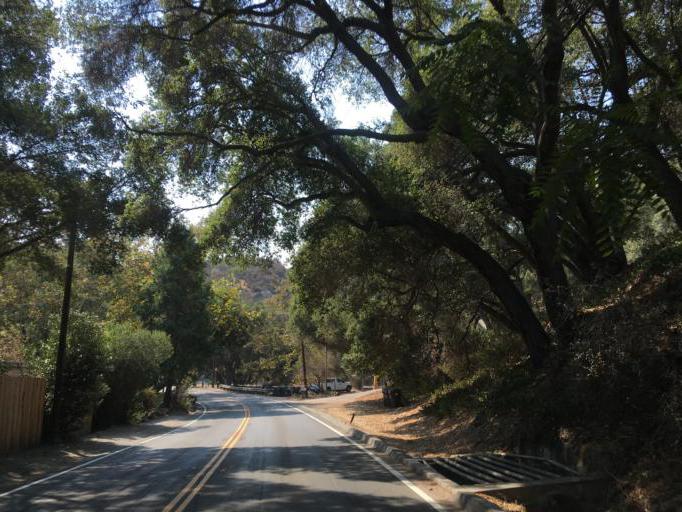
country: US
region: California
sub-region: Los Angeles County
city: Topanga
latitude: 34.1051
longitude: -118.6291
